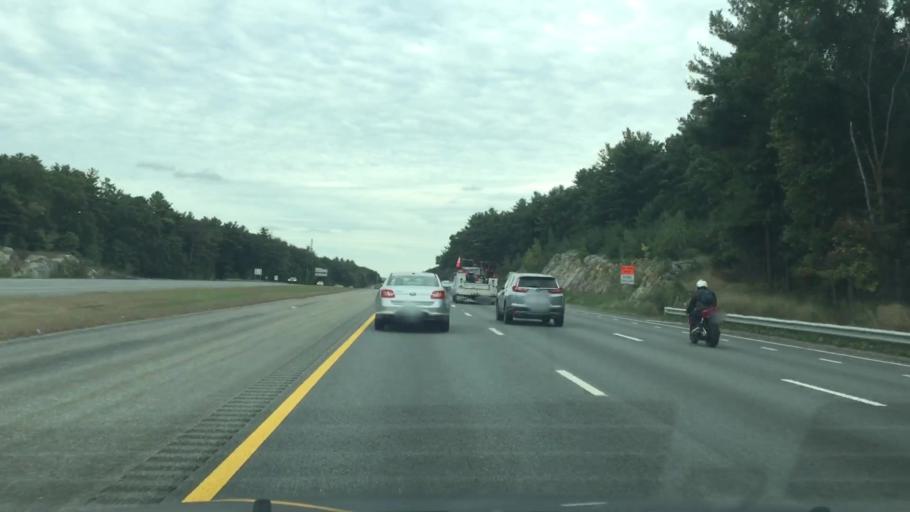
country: US
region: Massachusetts
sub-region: Middlesex County
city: Pinehurst
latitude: 42.5007
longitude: -71.2421
